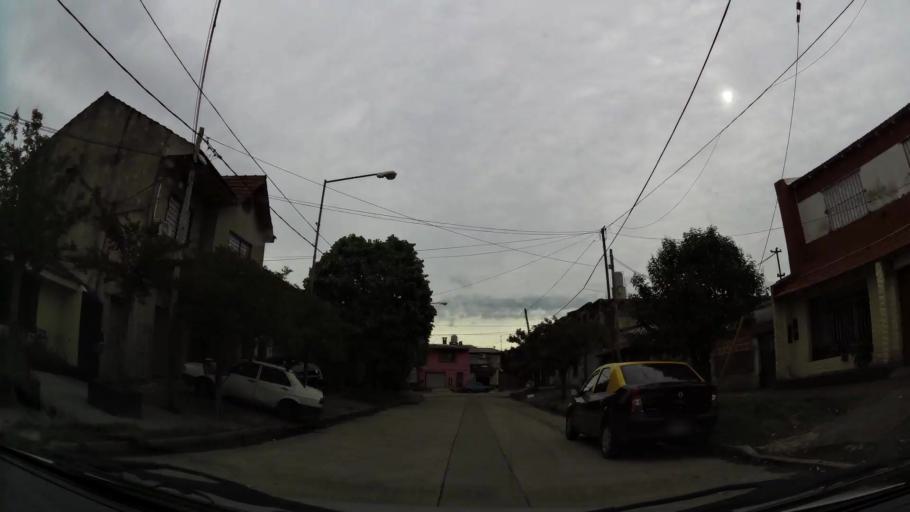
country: AR
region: Buenos Aires
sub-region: Partido de Lanus
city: Lanus
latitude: -34.7014
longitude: -58.3711
